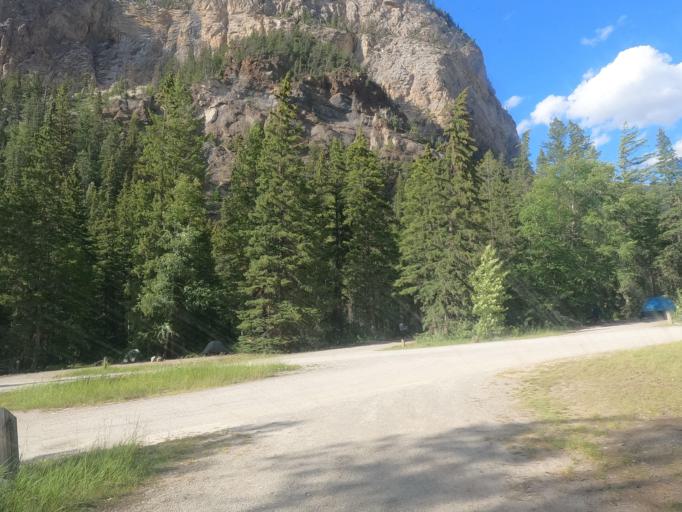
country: CA
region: Alberta
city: Lake Louise
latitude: 51.4212
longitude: -116.4435
